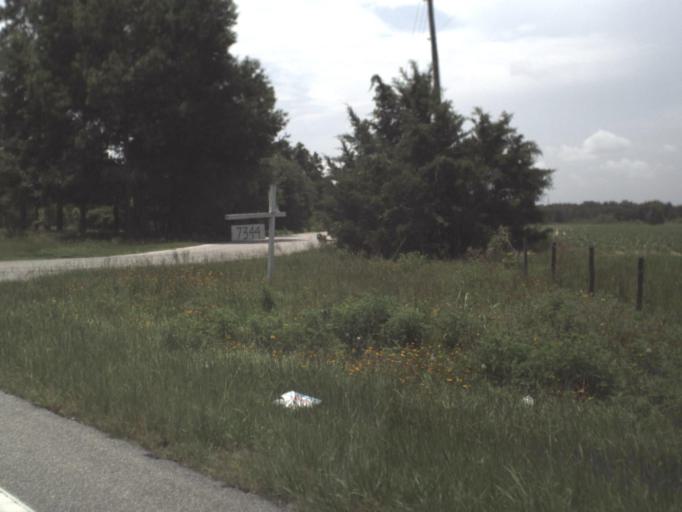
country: US
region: Florida
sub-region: Madison County
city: Madison
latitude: 30.4279
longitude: -83.3105
